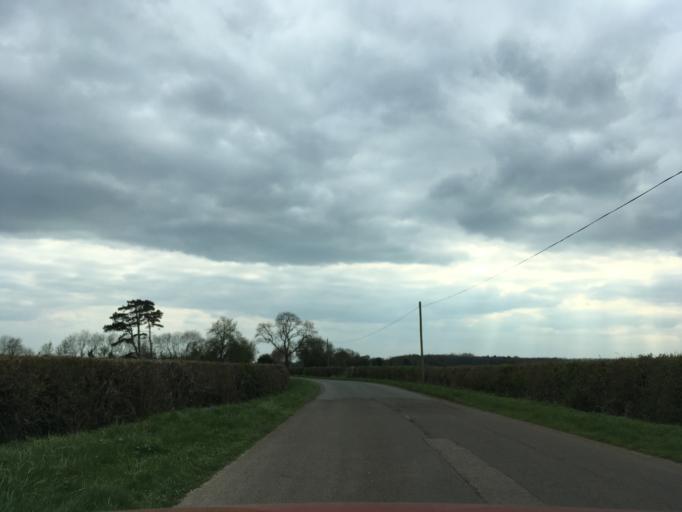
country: GB
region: England
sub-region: Oxfordshire
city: Bicester
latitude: 51.9385
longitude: -1.1368
